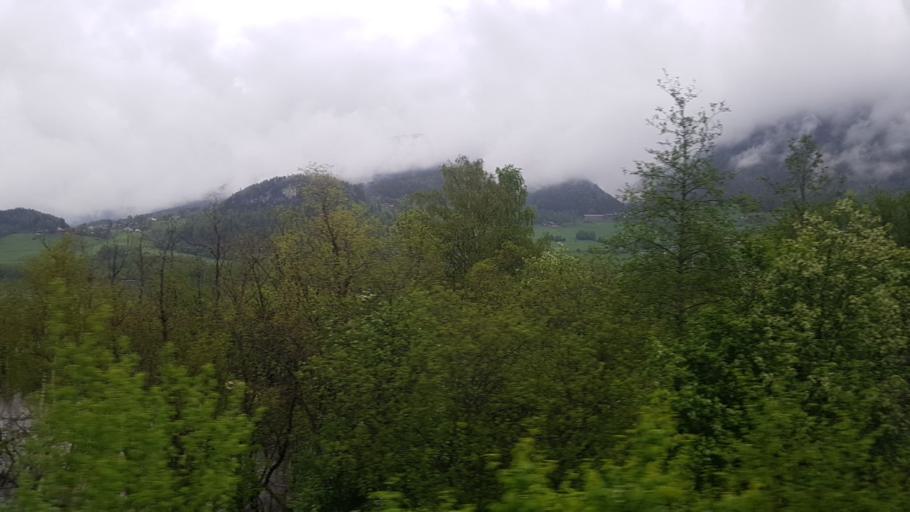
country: NO
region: Oppland
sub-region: Oyer
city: Tretten
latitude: 61.4029
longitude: 10.2412
